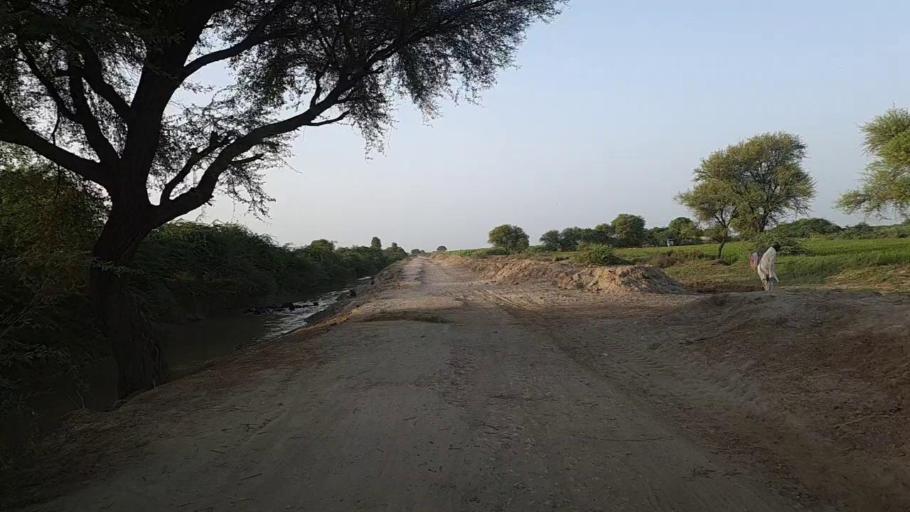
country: PK
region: Sindh
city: Kario
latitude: 24.7023
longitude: 68.4649
